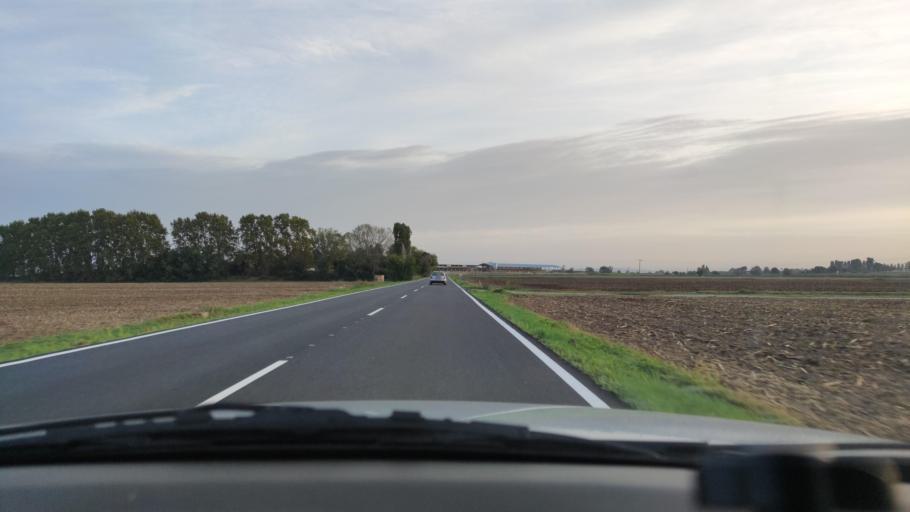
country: ES
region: Catalonia
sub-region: Provincia de Lleida
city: Mollerussa
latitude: 41.6553
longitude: 0.8907
